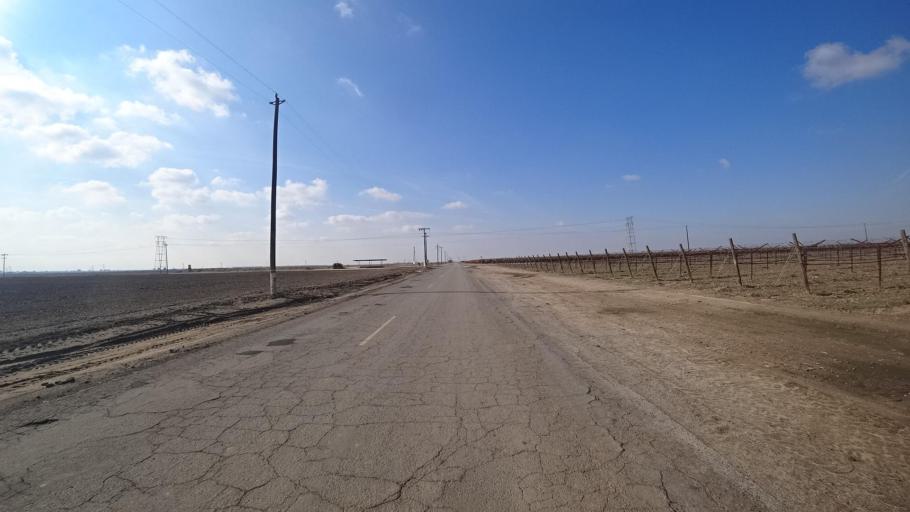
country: US
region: California
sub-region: Kern County
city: Arvin
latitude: 35.2530
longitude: -118.8054
